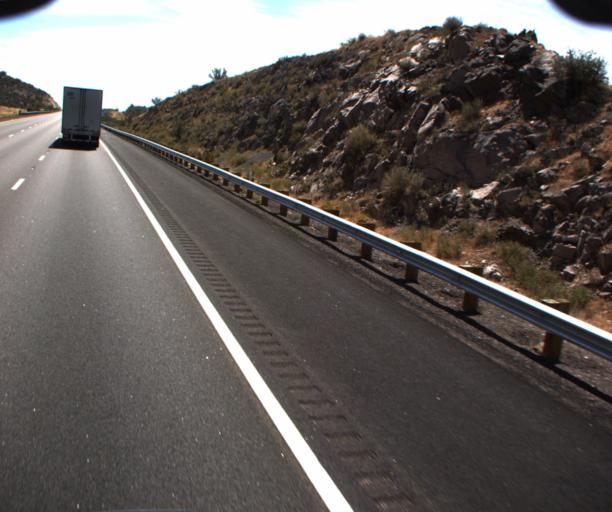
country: US
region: Arizona
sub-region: Mohave County
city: Peach Springs
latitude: 35.1875
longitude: -113.4167
